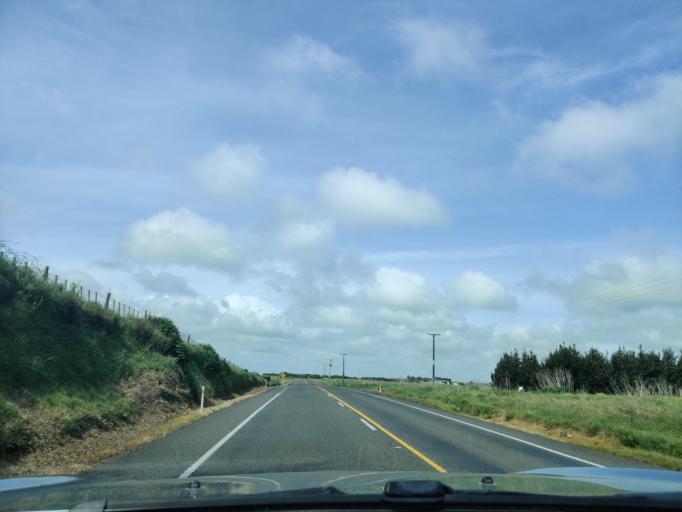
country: NZ
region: Taranaki
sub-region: South Taranaki District
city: Patea
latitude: -39.7669
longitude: 174.5529
